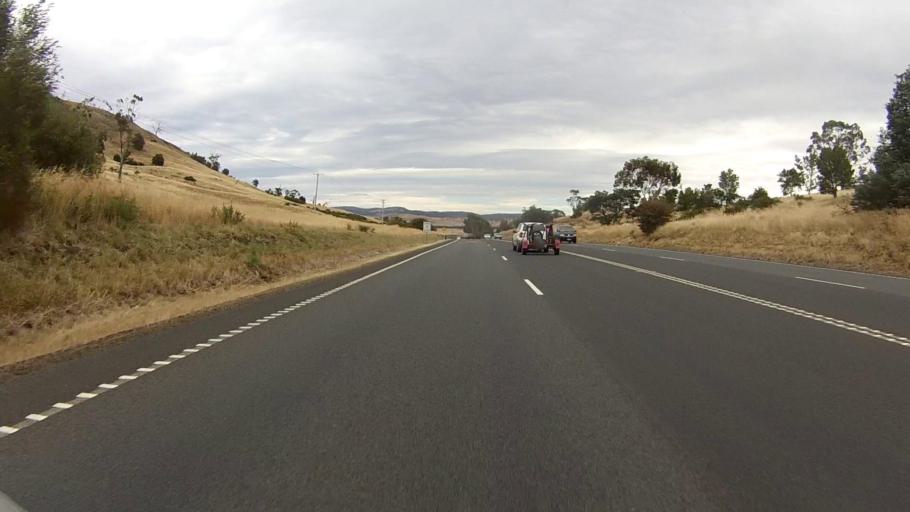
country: AU
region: Tasmania
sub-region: Brighton
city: Bridgewater
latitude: -42.3344
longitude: 147.3434
